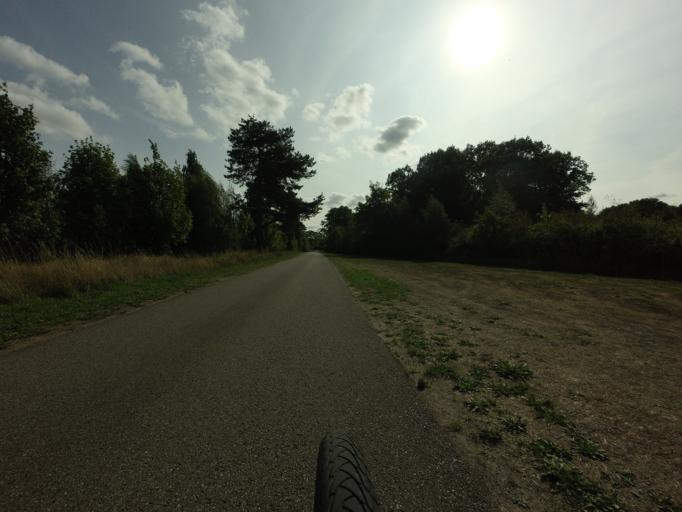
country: DK
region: Zealand
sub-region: Vordingborg Kommune
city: Praesto
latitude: 55.1714
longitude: 12.0986
